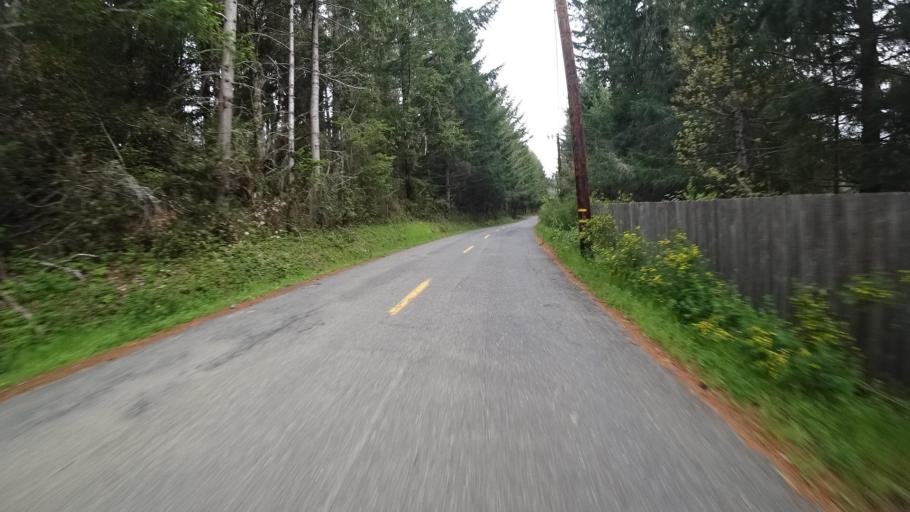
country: US
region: California
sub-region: Humboldt County
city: Redway
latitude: 40.2948
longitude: -123.8200
